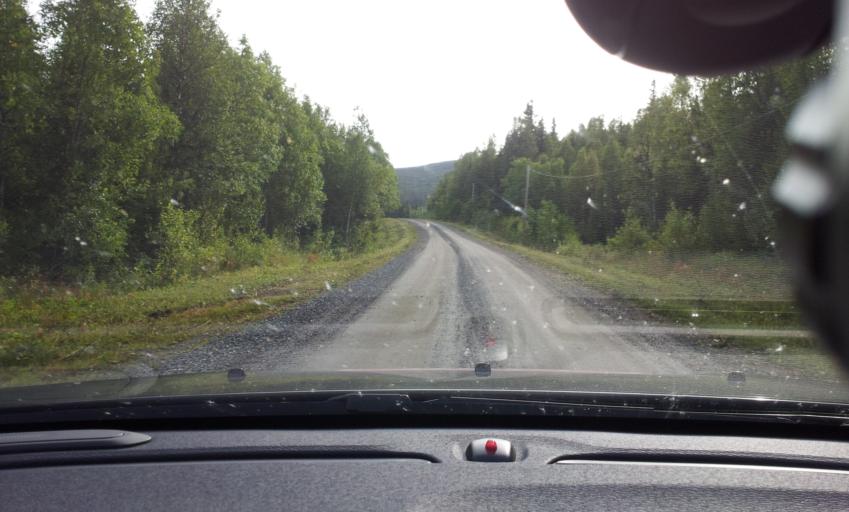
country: SE
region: Jaemtland
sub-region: Are Kommun
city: Are
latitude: 63.6751
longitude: 12.8157
